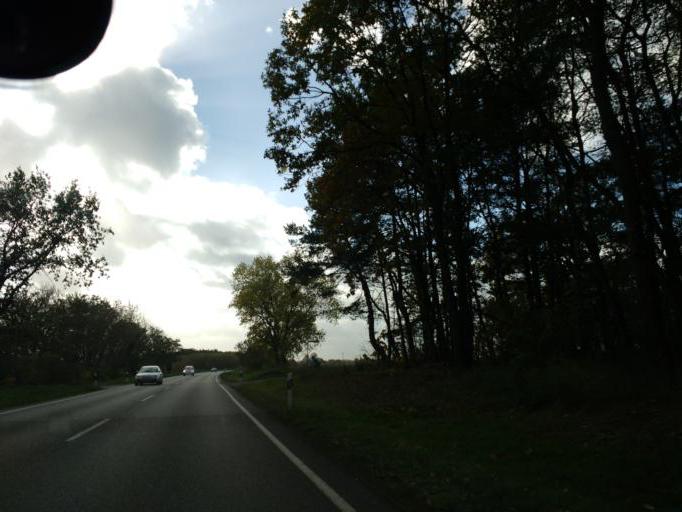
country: DE
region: Brandenburg
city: Petershagen
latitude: 52.5018
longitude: 13.7954
